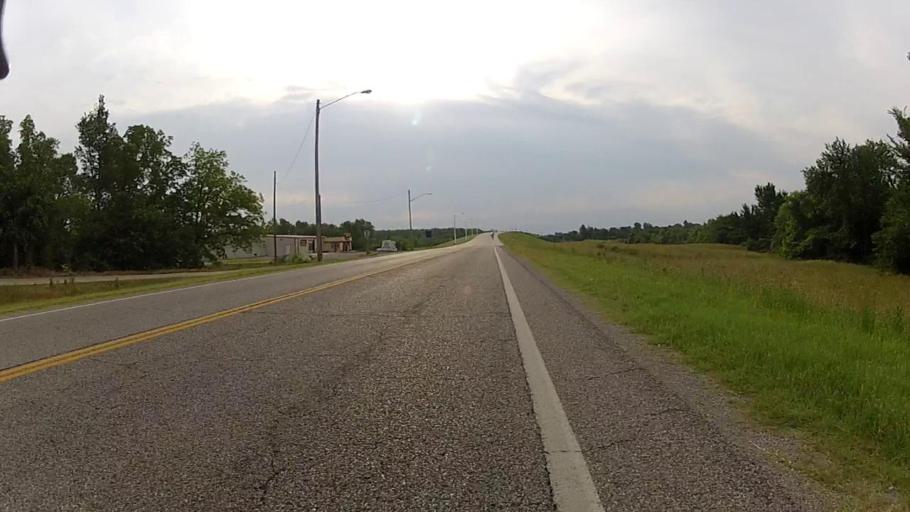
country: US
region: Kansas
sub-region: Cherokee County
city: Columbus
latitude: 37.1788
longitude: -94.8414
